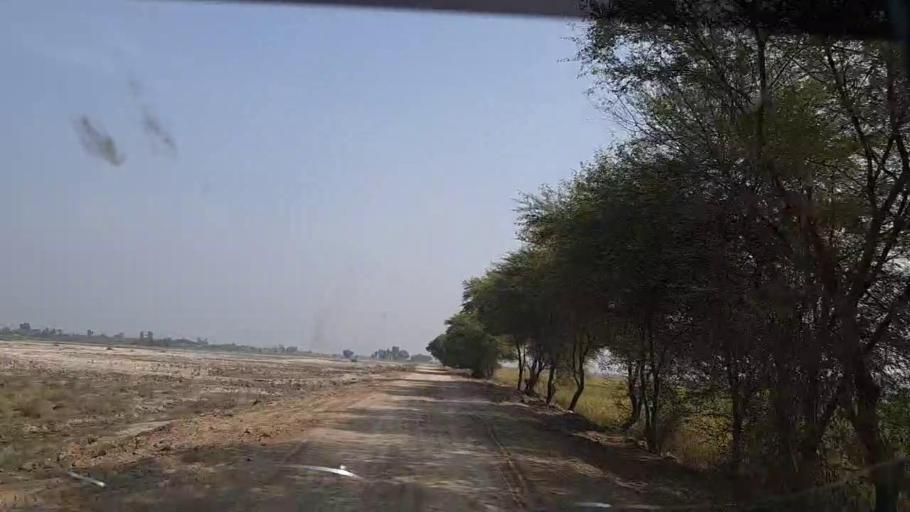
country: PK
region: Sindh
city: Shikarpur
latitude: 28.0513
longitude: 68.6661
